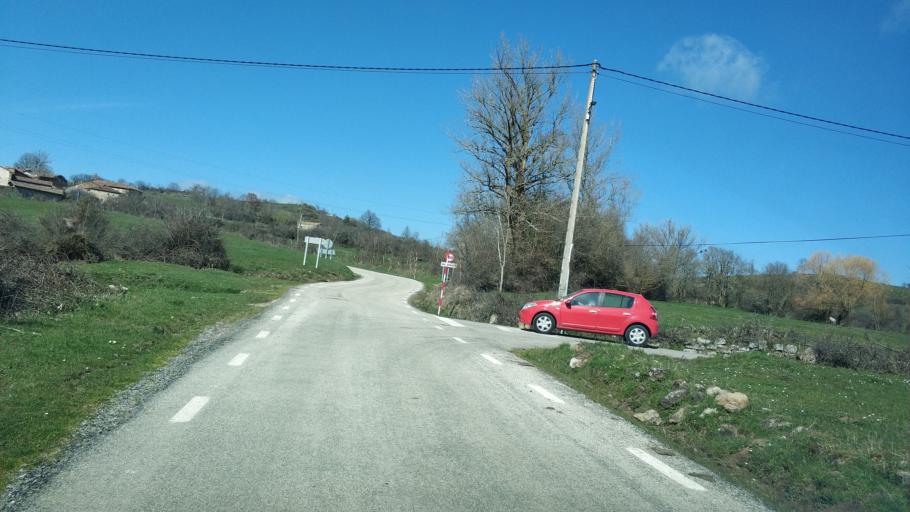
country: ES
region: Cantabria
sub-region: Provincia de Cantabria
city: Mataporquera
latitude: 42.8747
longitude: -4.0886
